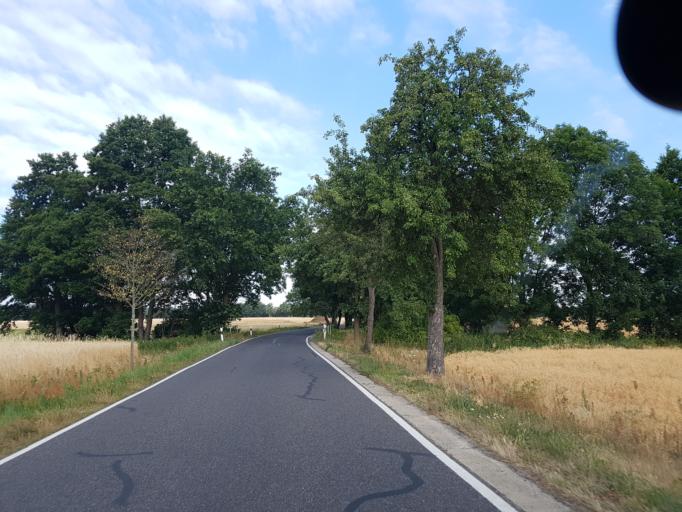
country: DE
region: Brandenburg
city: Luckau
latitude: 51.8428
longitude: 13.6310
